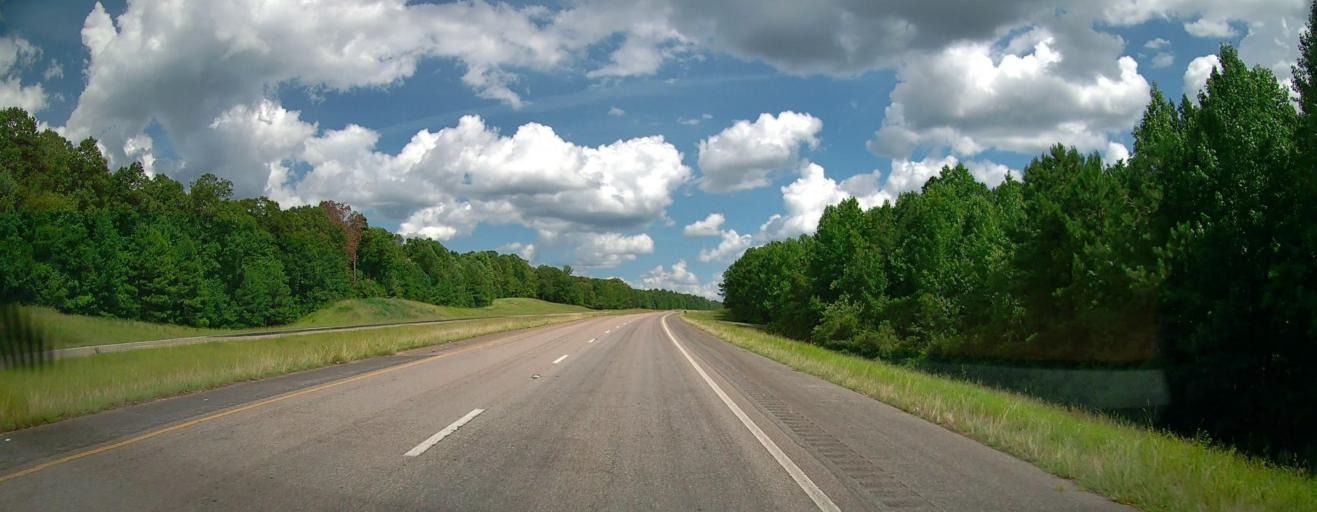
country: US
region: Mississippi
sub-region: Lowndes County
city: New Hope
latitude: 33.4677
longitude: -88.2343
